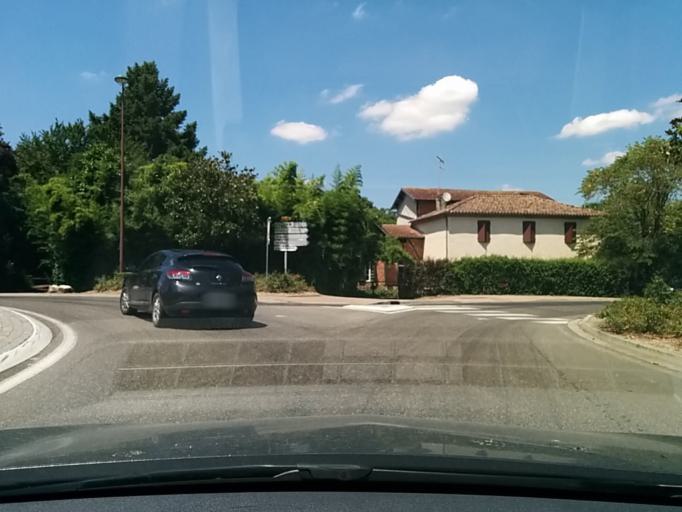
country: FR
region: Midi-Pyrenees
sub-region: Departement du Gers
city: Vic-Fezensac
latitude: 43.7557
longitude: 0.2946
